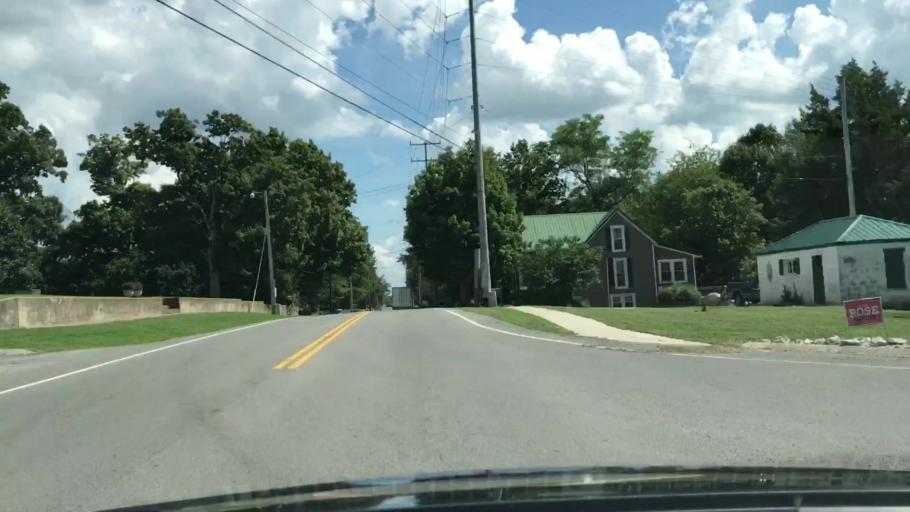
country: US
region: Tennessee
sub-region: Robertson County
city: Cross Plains
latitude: 36.5490
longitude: -86.7027
